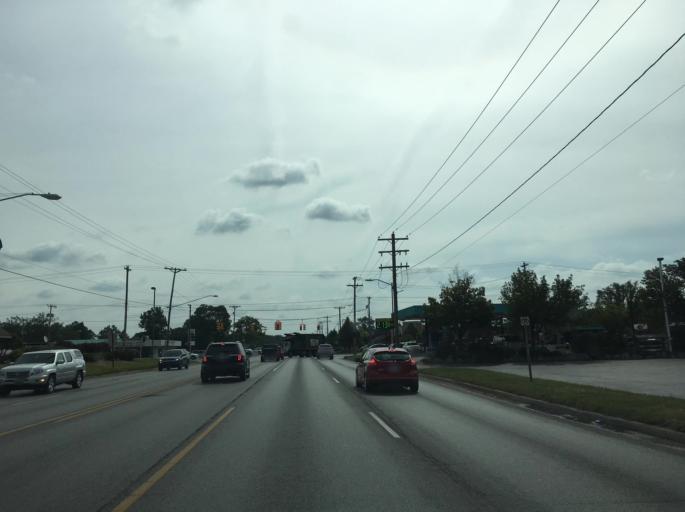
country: US
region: Michigan
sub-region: Grand Traverse County
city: Traverse City
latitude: 44.7333
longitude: -85.5968
